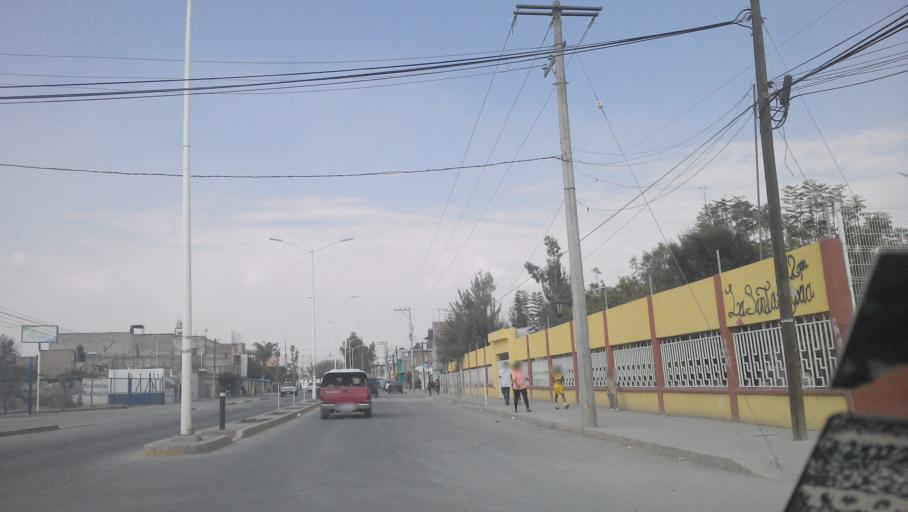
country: MX
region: Guanajuato
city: San Francisco del Rincon
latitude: 21.0066
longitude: -101.8516
